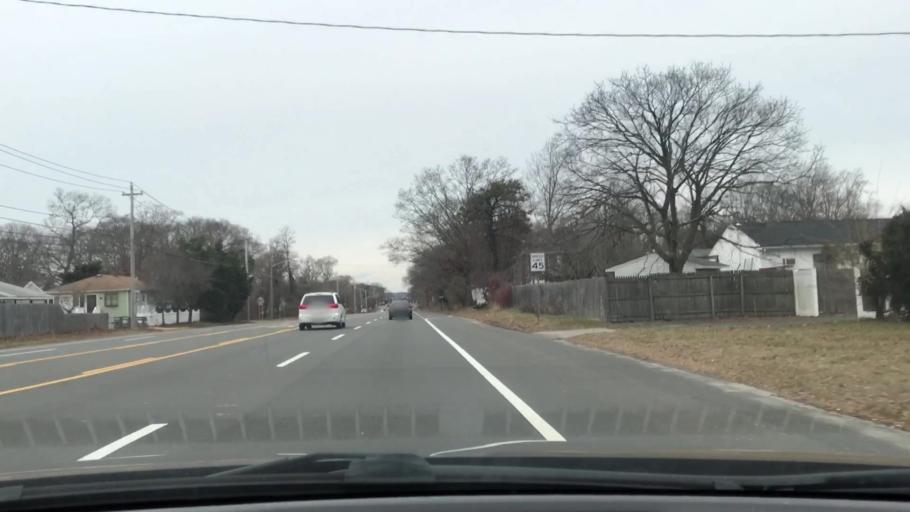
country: US
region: New York
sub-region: Suffolk County
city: North Patchogue
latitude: 40.7879
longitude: -73.0165
